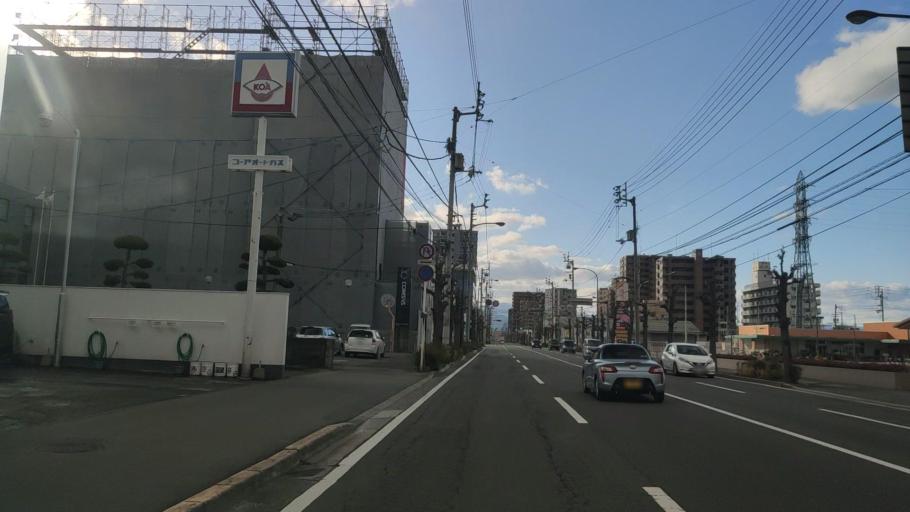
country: JP
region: Ehime
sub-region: Shikoku-chuo Shi
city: Matsuyama
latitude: 33.8369
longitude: 132.7525
